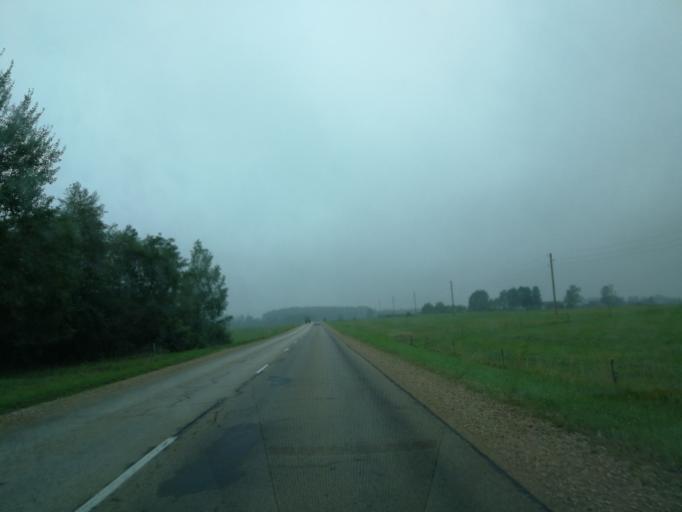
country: LV
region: Preilu Rajons
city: Preili
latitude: 56.2984
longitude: 26.6663
